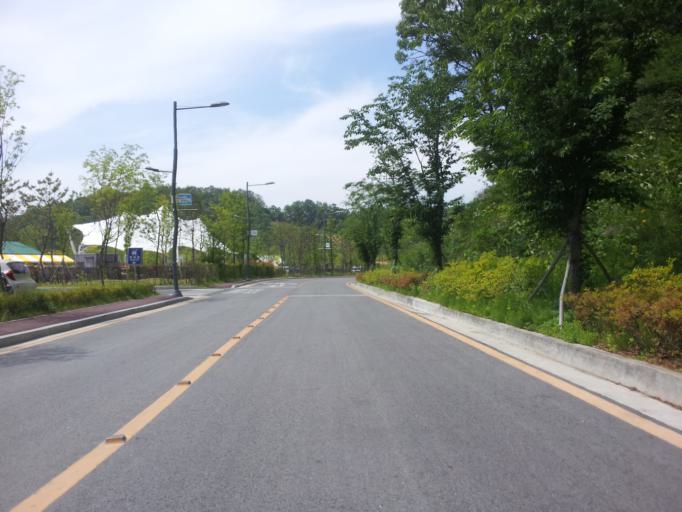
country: KR
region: Daejeon
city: Sintansin
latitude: 36.4554
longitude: 127.4757
